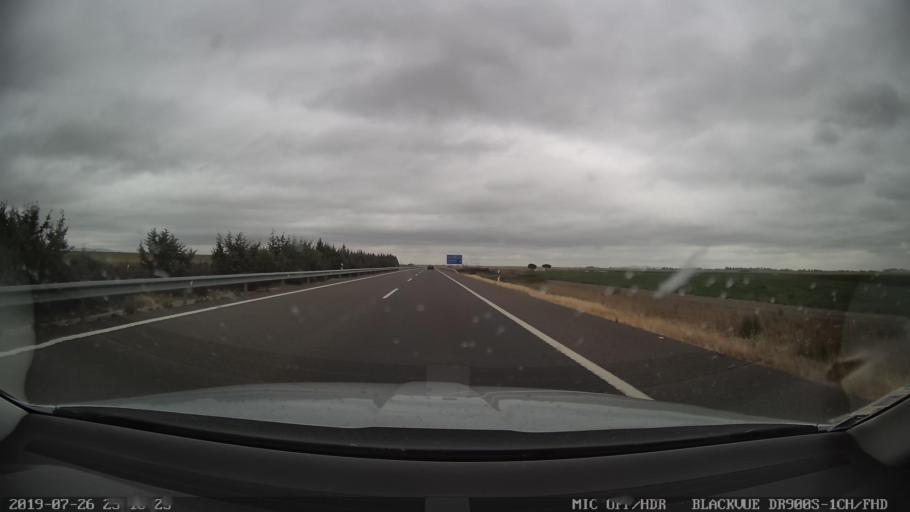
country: ES
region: Extremadura
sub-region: Provincia de Badajoz
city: Santa Amalia
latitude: 39.0677
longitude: -6.0466
